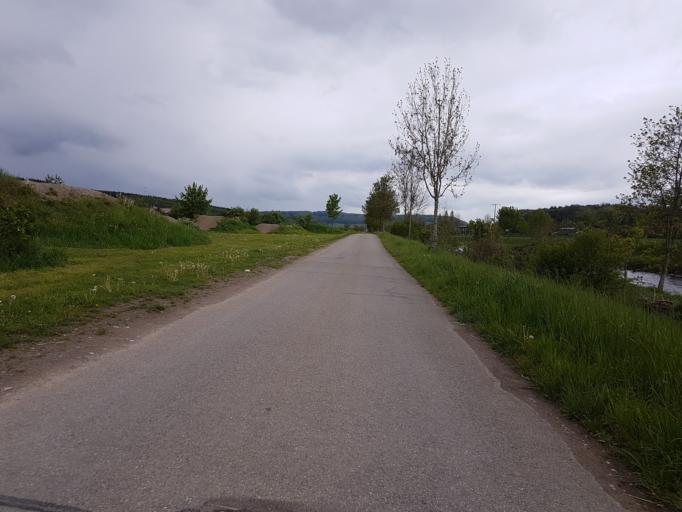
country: DE
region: Baden-Wuerttemberg
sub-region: Freiburg Region
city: Wutoschingen
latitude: 47.6508
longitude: 8.3565
